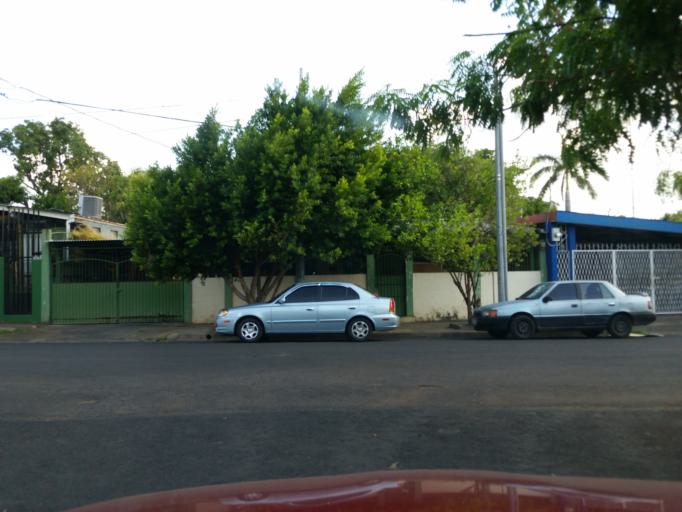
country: NI
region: Managua
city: Managua
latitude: 12.1281
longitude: -86.2591
